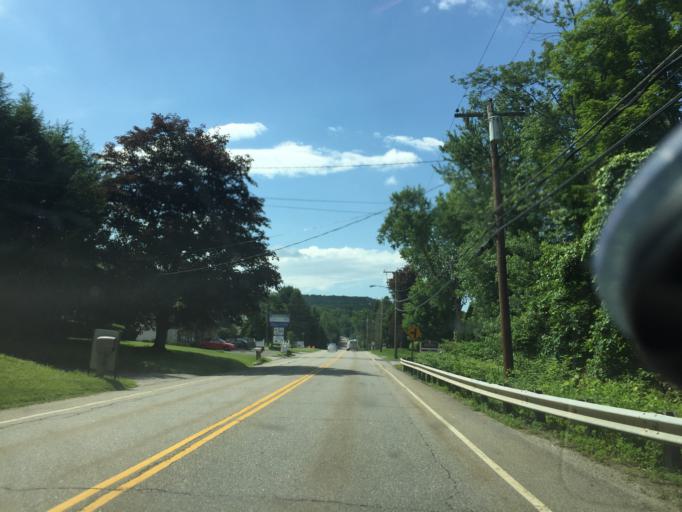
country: US
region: Connecticut
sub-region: Litchfield County
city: West Torrington
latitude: 41.8203
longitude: -73.1537
